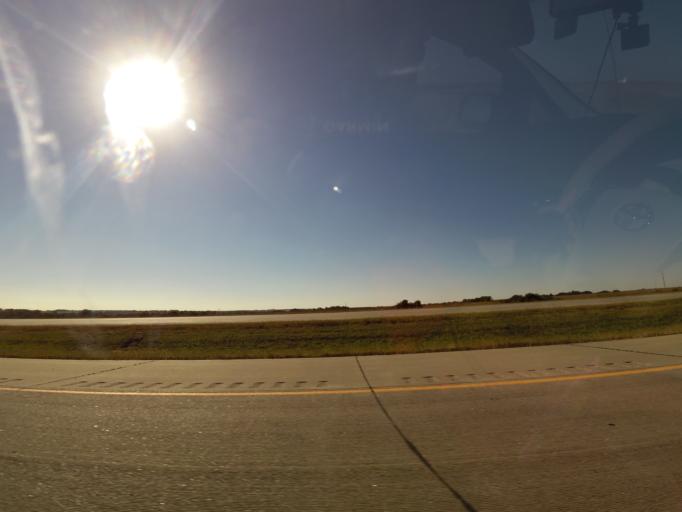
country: US
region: Nebraska
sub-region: Lancaster County
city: Waverly
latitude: 40.9096
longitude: -96.4914
